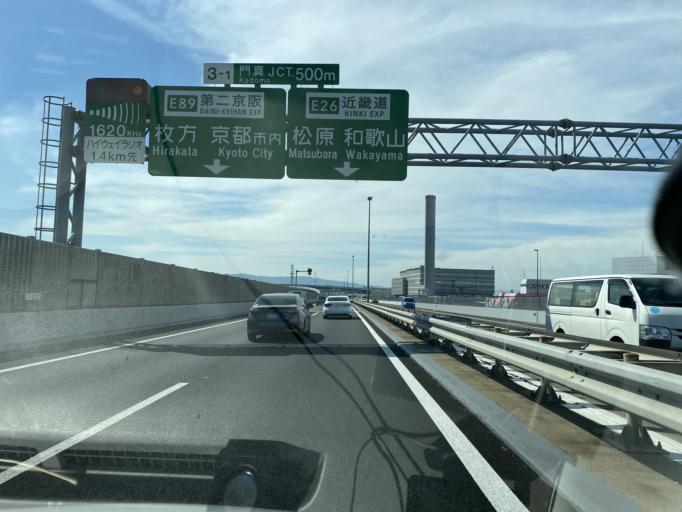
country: JP
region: Osaka
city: Kadoma
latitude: 34.7233
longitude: 135.5847
